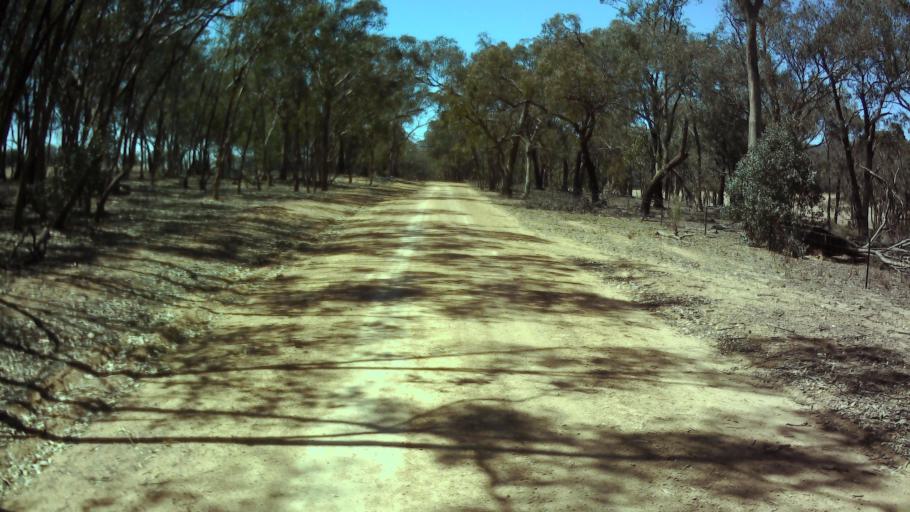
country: AU
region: New South Wales
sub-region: Weddin
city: Grenfell
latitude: -33.9608
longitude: 148.0874
